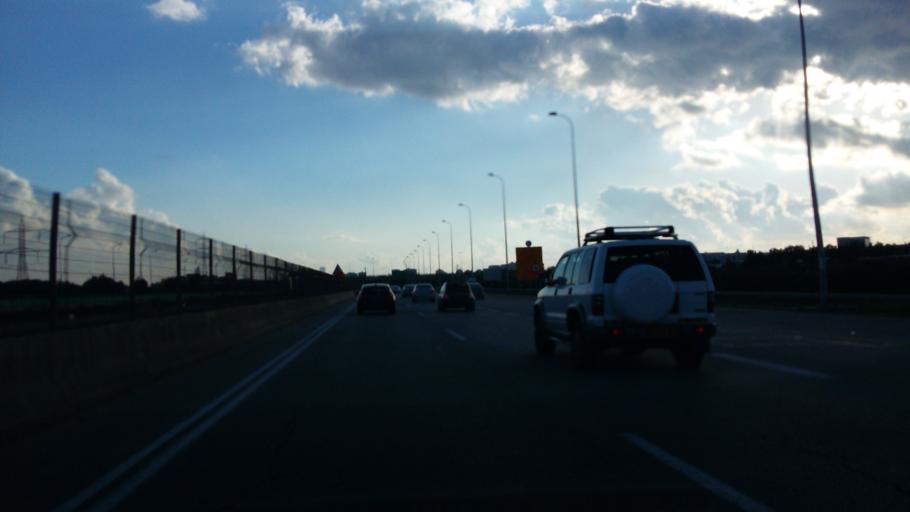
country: IL
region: Tel Aviv
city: Herzliya Pituah
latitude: 32.1474
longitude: 34.8057
